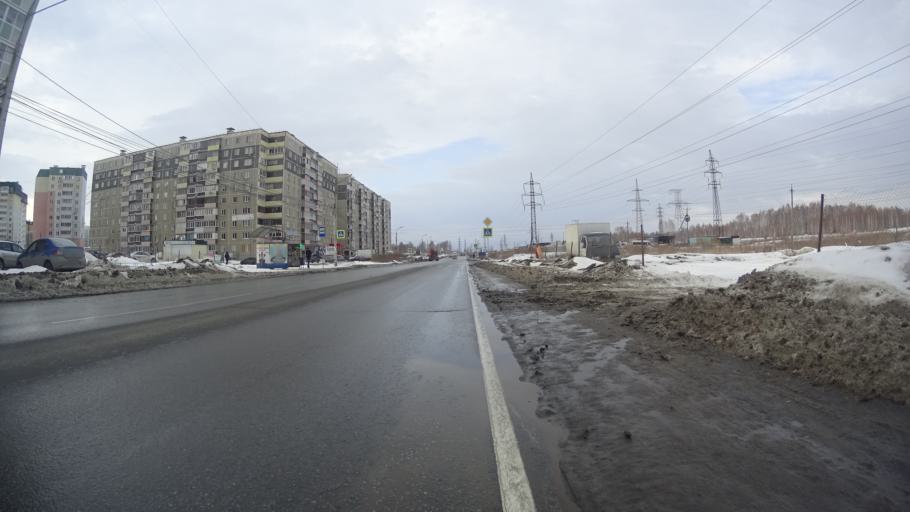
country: RU
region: Chelyabinsk
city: Roshchino
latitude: 55.2179
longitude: 61.3004
